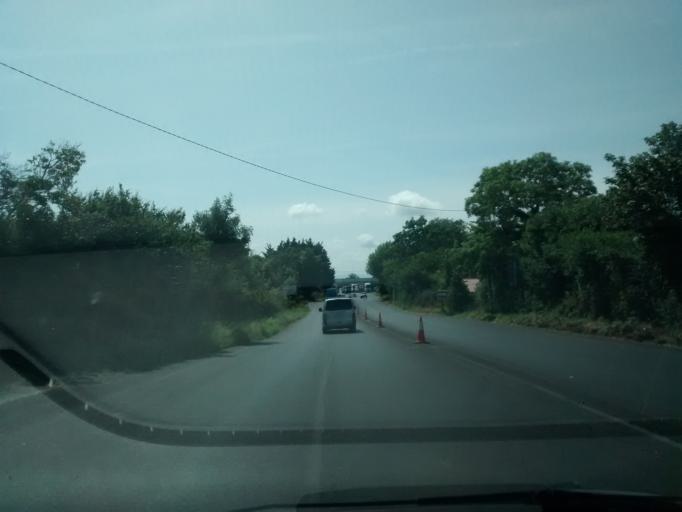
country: IE
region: Leinster
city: Lusk
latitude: 53.5079
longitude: -6.1929
